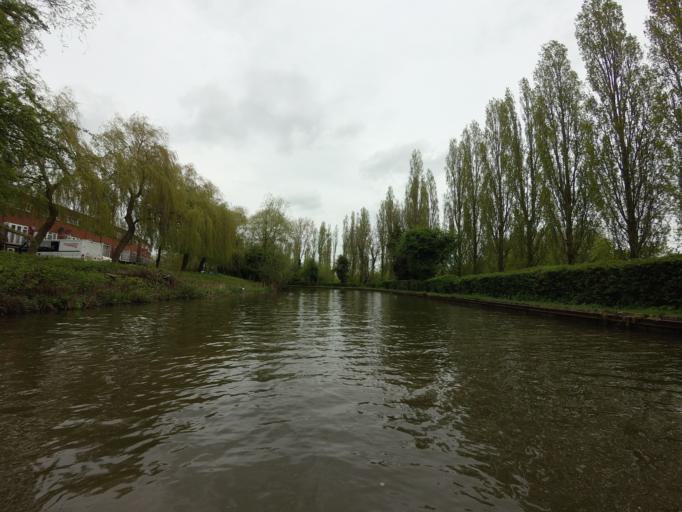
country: GB
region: England
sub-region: Milton Keynes
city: Milton Keynes
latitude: 52.0338
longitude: -0.7304
